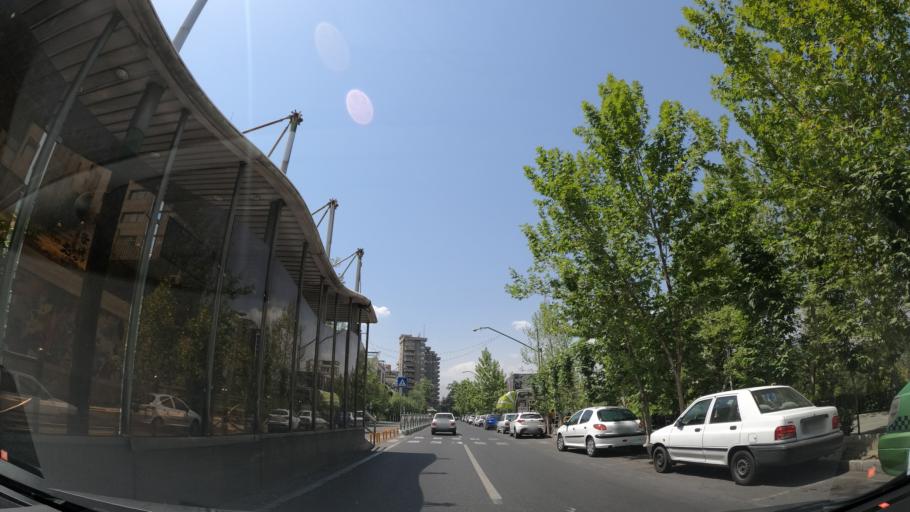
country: IR
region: Tehran
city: Tehran
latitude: 35.7351
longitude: 51.4099
